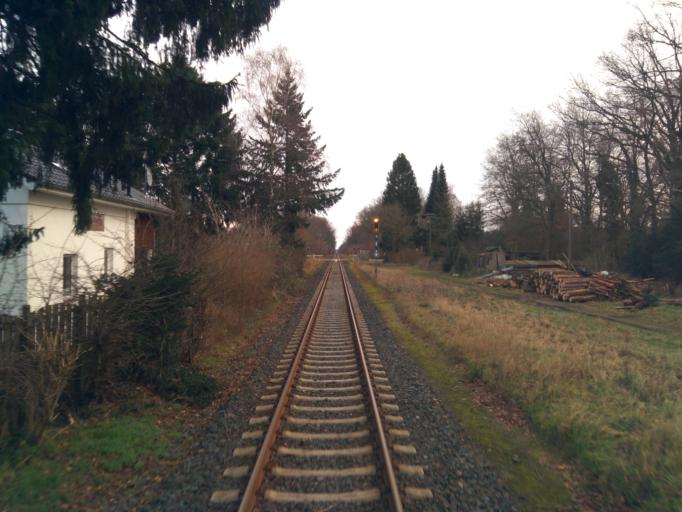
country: DE
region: Lower Saxony
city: Wriedel
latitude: 53.0023
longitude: 10.2602
